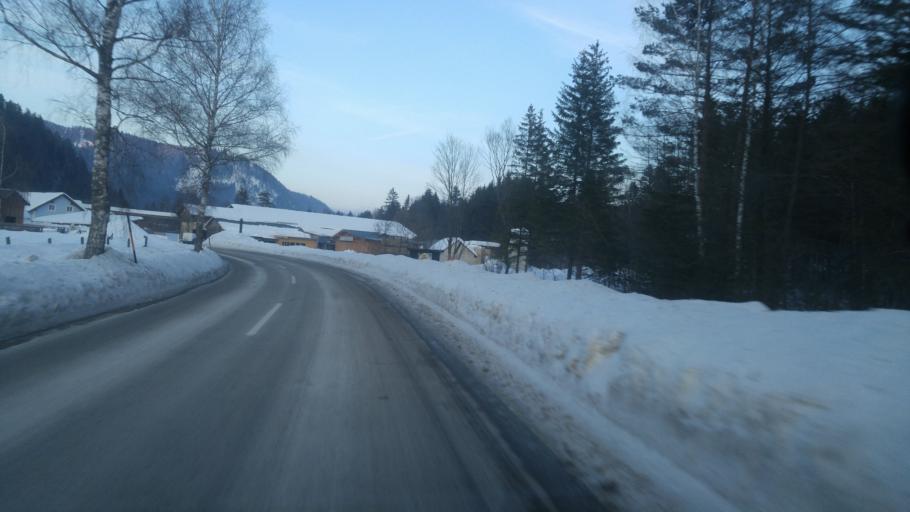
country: AT
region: Lower Austria
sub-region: Politischer Bezirk Wiener Neustadt
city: Rohr im Gebirge
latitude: 47.8811
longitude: 15.7110
